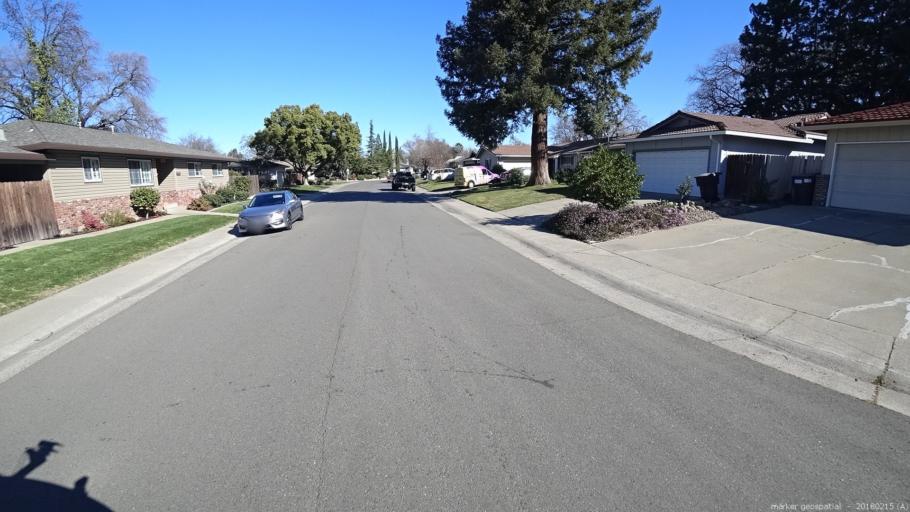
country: US
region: California
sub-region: Sacramento County
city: Foothill Farms
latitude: 38.6631
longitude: -121.3351
